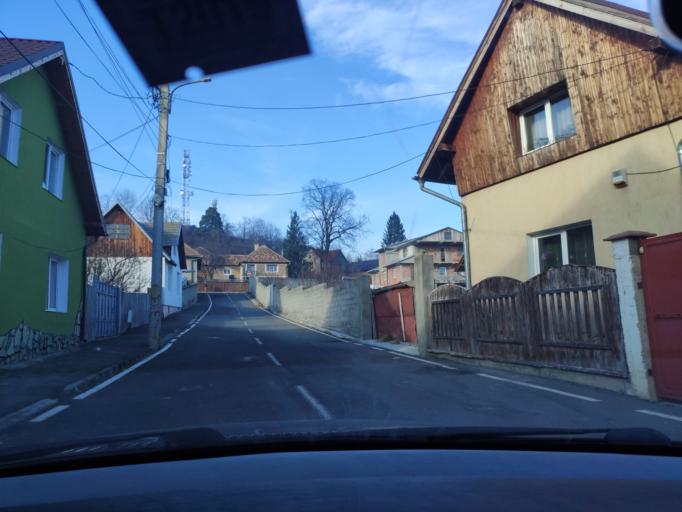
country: RO
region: Brasov
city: Codlea
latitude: 45.6933
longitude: 25.4428
